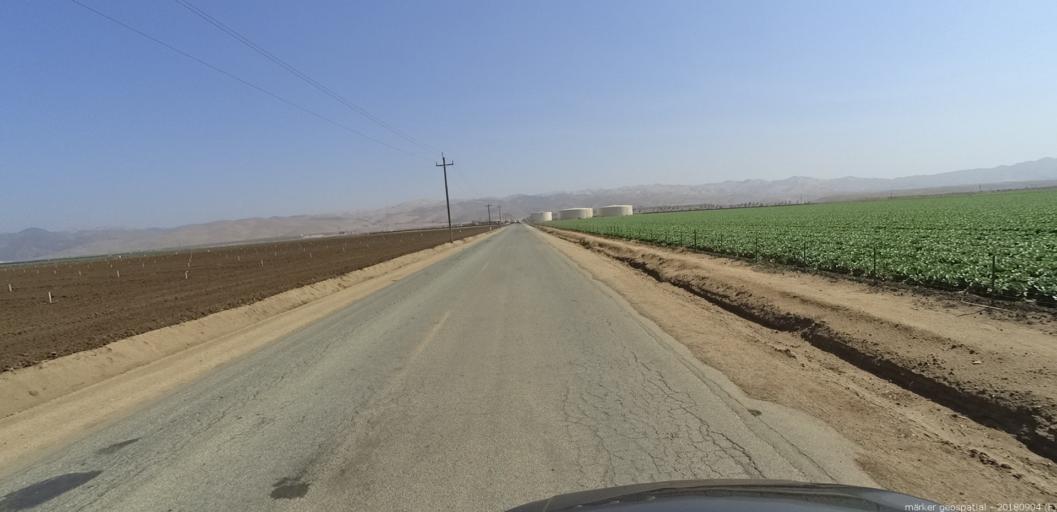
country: US
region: California
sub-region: Monterey County
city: Gonzales
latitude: 36.5233
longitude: -121.4227
